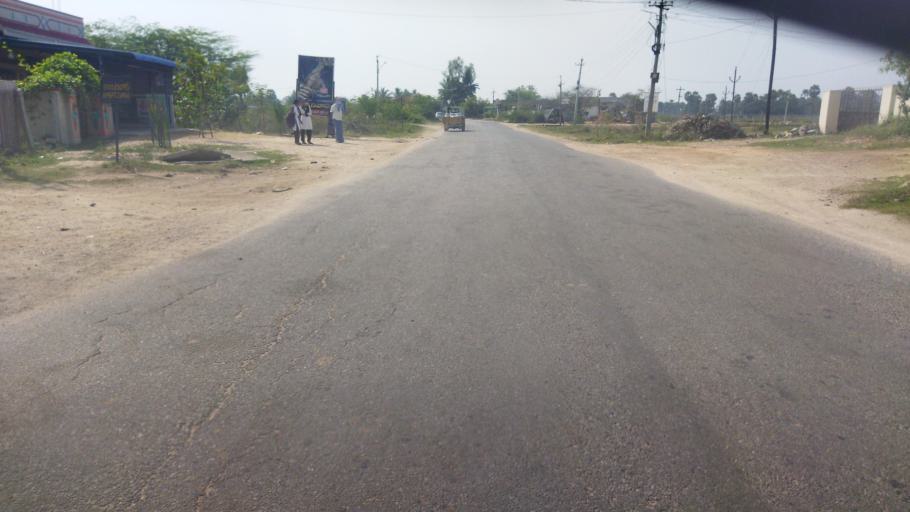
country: IN
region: Telangana
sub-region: Nalgonda
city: Nalgonda
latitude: 17.1529
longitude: 79.3109
